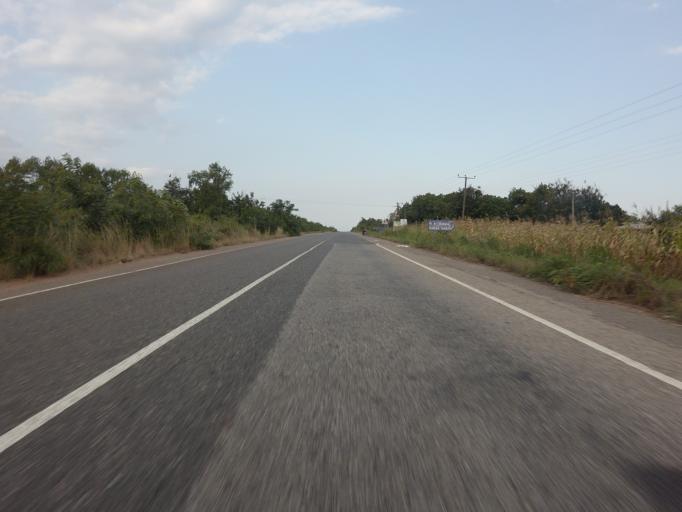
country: GH
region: Volta
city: Anloga
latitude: 6.0858
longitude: 0.5514
